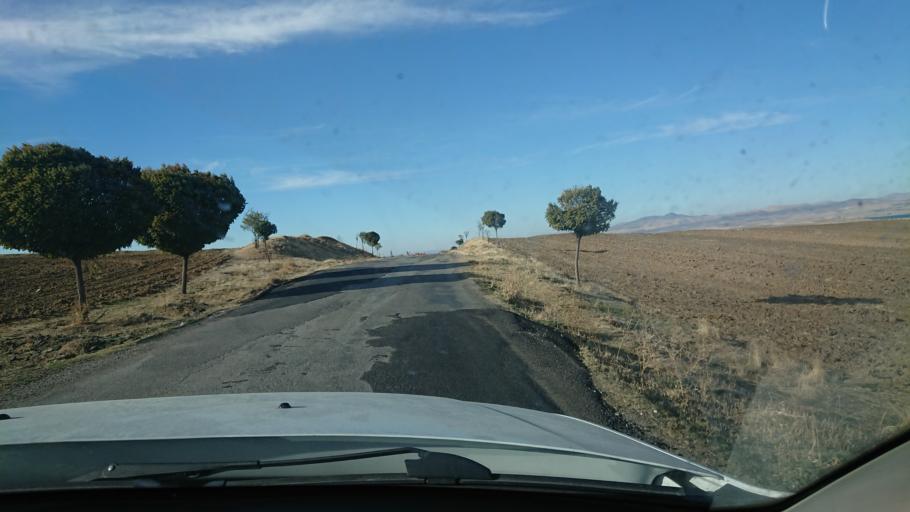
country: TR
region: Aksaray
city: Sariyahsi
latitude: 38.9733
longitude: 33.8596
